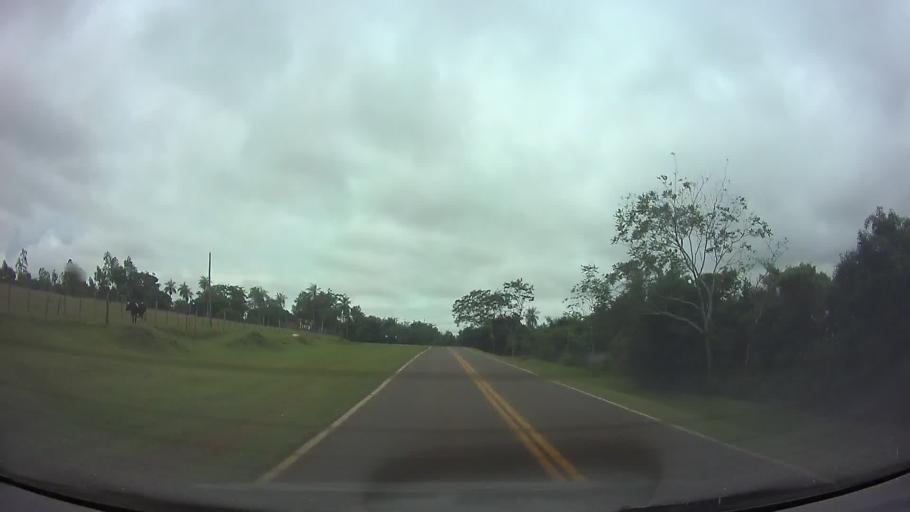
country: PY
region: Paraguari
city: Acahay
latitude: -25.9246
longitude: -57.1070
